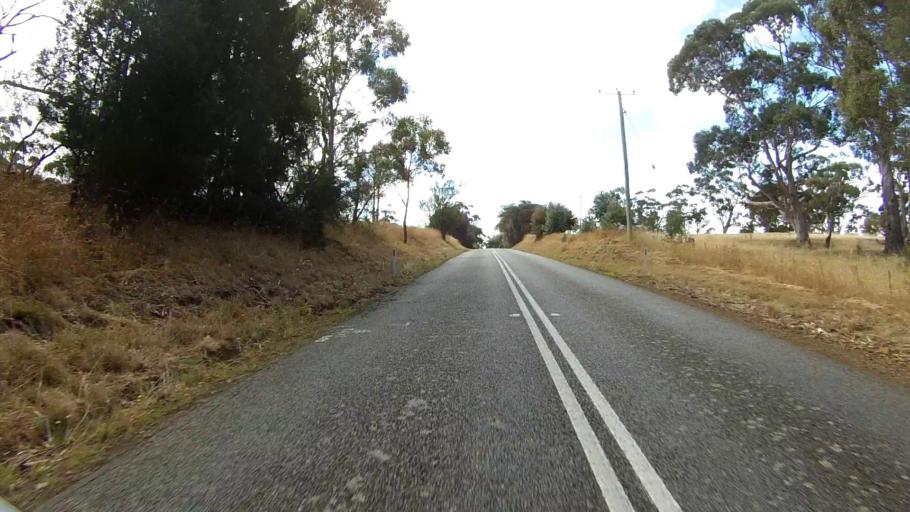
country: AU
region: Tasmania
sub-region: Sorell
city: Sorell
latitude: -42.2598
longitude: 148.0030
